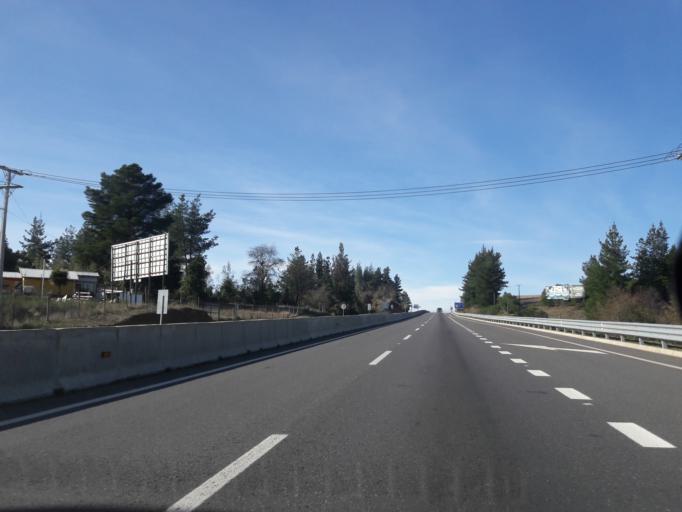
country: CL
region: Biobio
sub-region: Provincia de Biobio
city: Yumbel
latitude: -36.9624
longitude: -72.7154
